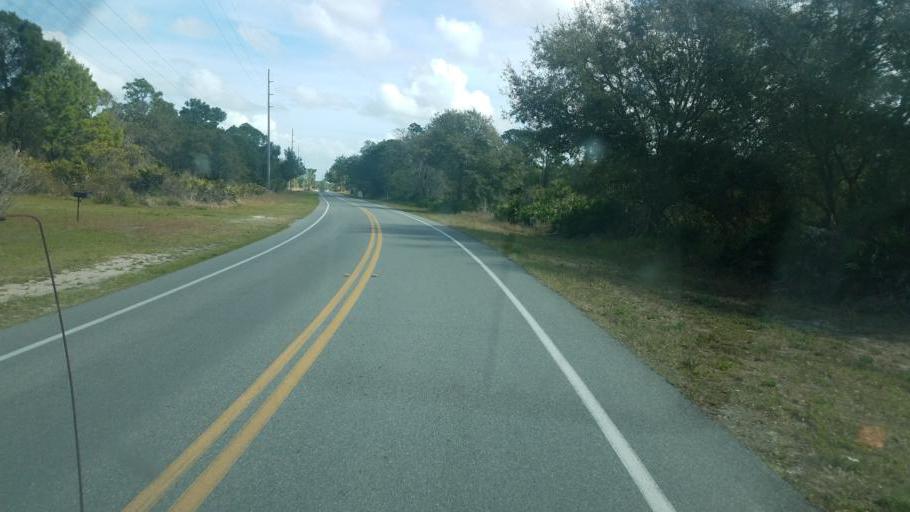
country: US
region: Florida
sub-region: Polk County
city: Babson Park
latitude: 27.9275
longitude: -81.4520
